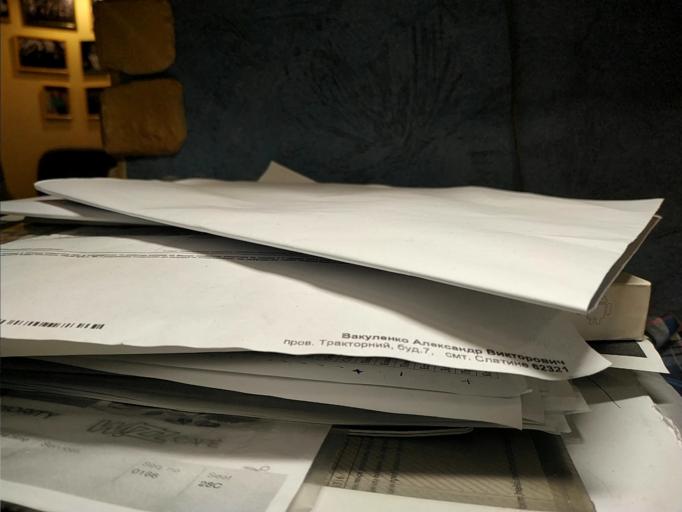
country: RU
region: Tverskaya
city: Zubtsov
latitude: 56.0953
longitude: 34.7158
